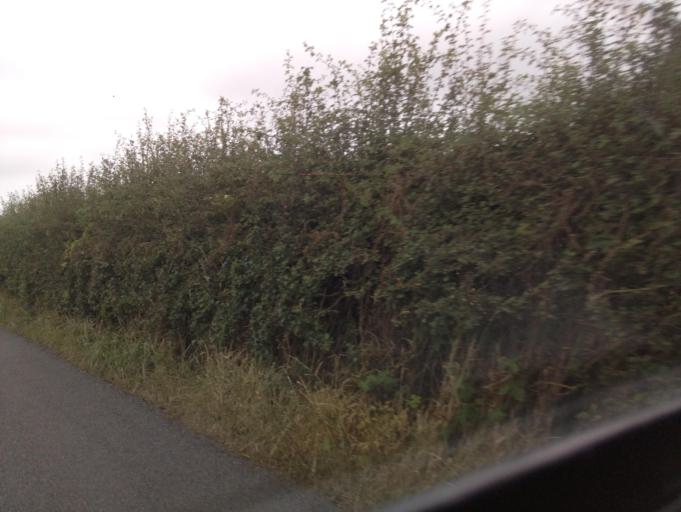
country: GB
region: England
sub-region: Leicestershire
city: Ashby de la Zouch
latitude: 52.7729
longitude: -1.5049
